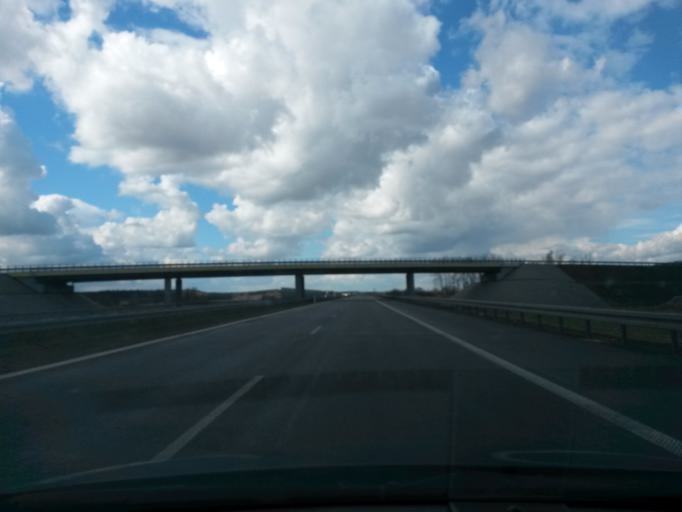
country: PL
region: Greater Poland Voivodeship
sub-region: Powiat kolski
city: Dabie
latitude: 52.1056
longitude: 18.7527
